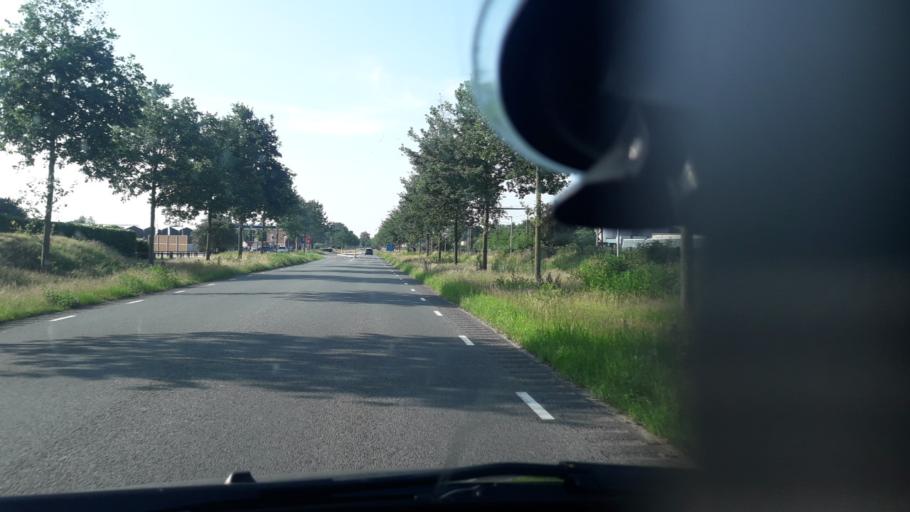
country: NL
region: Gelderland
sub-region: Gemeente Ermelo
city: Ermelo
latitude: 52.3161
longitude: 5.6147
